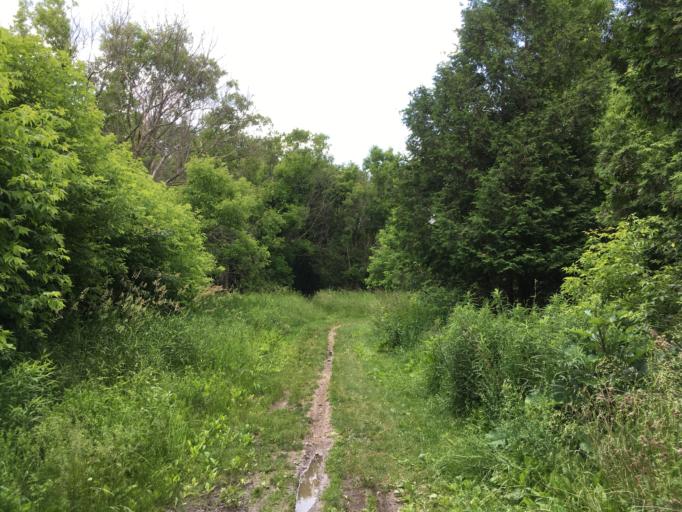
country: CA
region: Ontario
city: Oshawa
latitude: 43.8760
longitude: -78.8541
